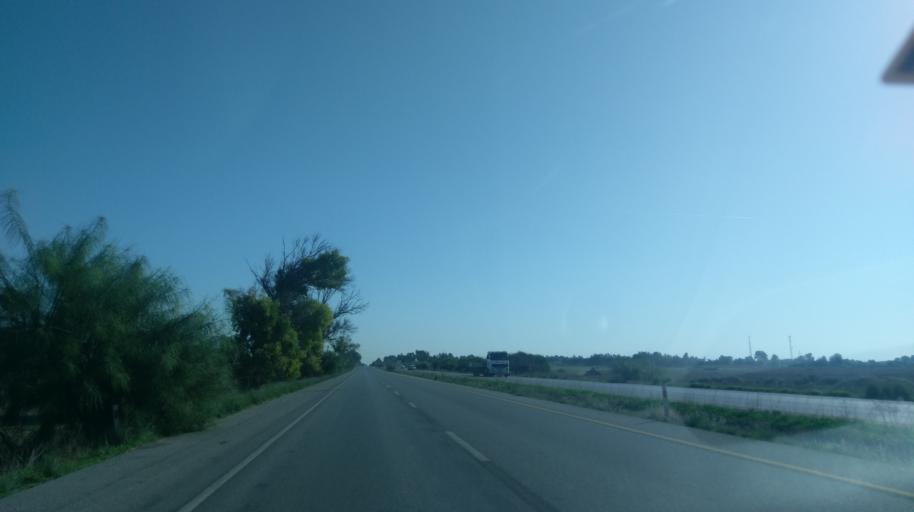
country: CY
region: Larnaka
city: Athienou
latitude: 35.2094
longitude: 33.5758
